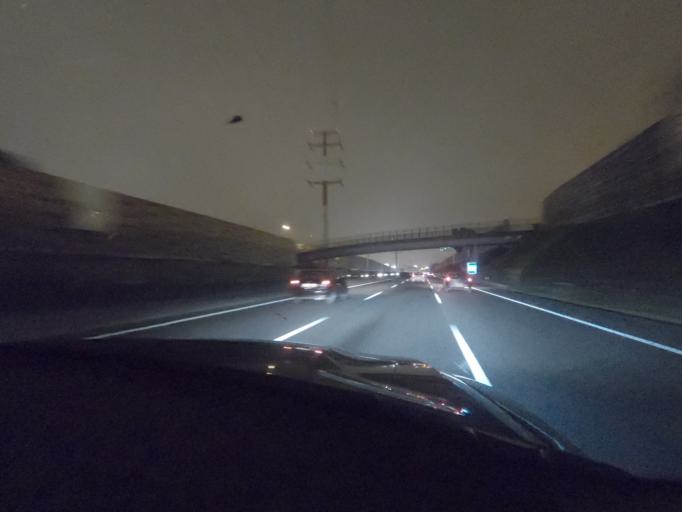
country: PT
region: Lisbon
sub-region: Loures
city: Sao Joao da Talha
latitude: 38.8195
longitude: -9.1002
